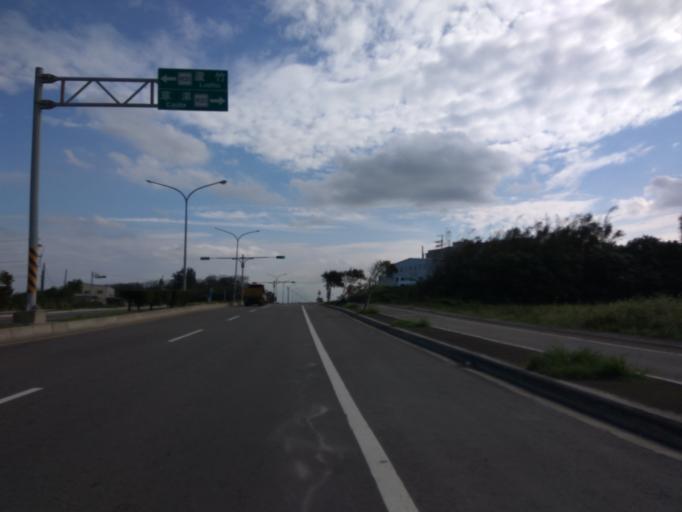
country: TW
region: Taiwan
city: Taoyuan City
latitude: 25.0782
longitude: 121.1696
